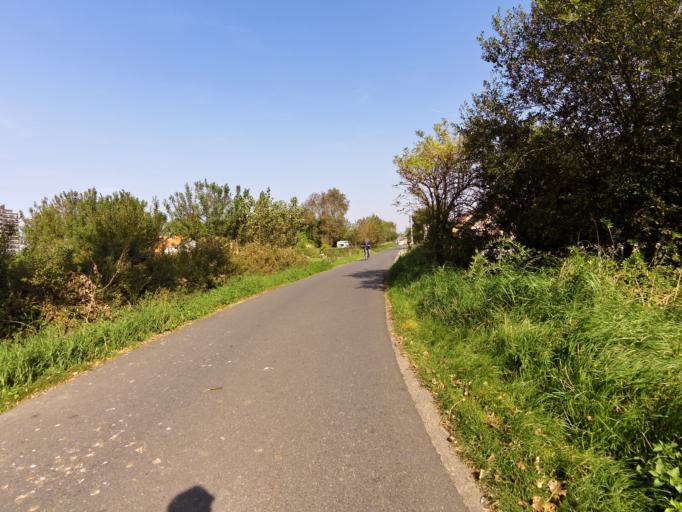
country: BE
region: Flanders
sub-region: Provincie West-Vlaanderen
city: Middelkerke
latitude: 51.1764
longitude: 2.7948
